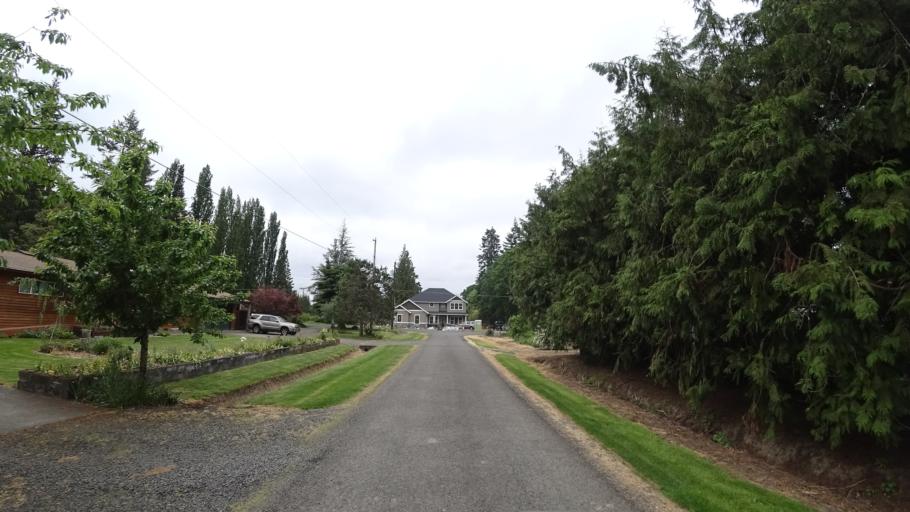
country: US
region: Oregon
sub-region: Washington County
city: Rockcreek
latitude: 45.5733
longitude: -122.8955
